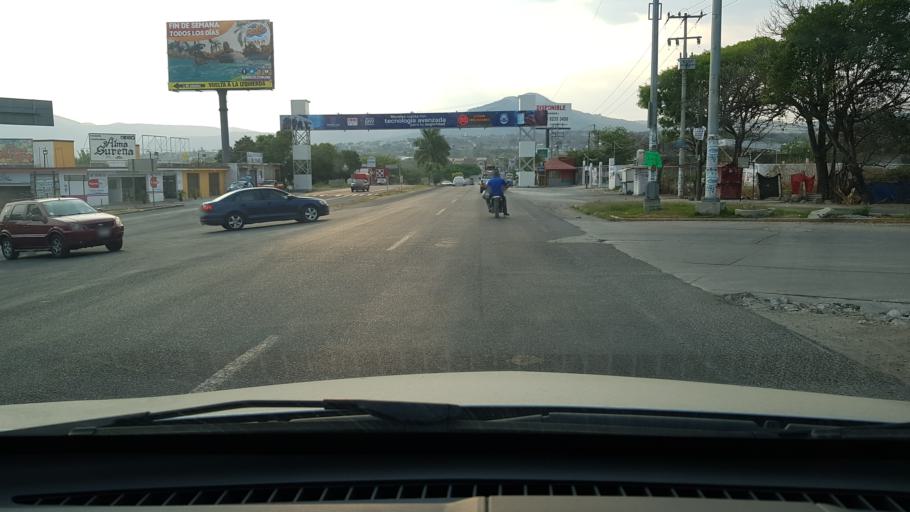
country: MX
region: Morelos
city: Yautepec
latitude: 18.8704
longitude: -99.0673
